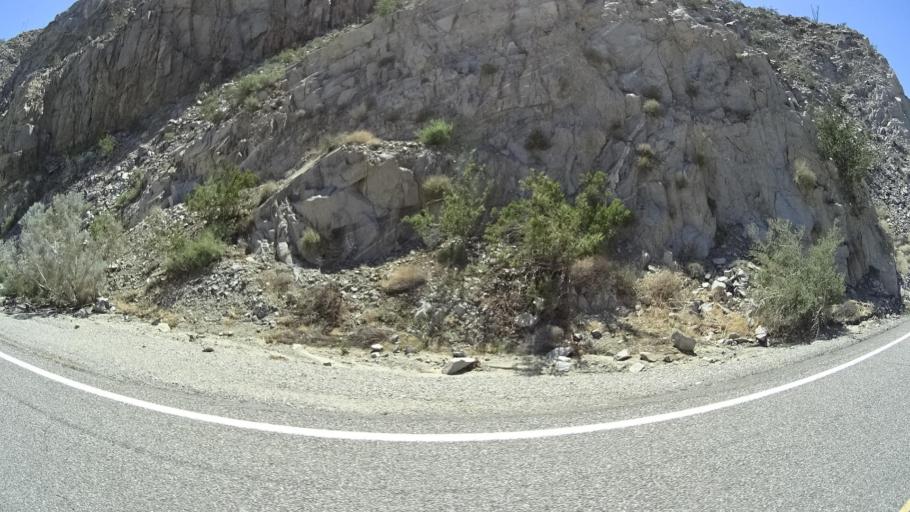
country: US
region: California
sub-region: San Diego County
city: Borrego Springs
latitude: 33.1353
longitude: -116.2985
